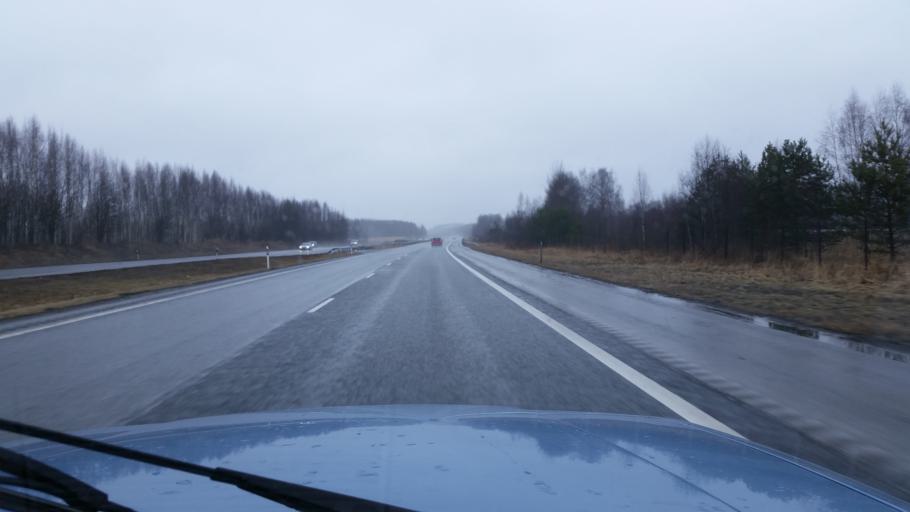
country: FI
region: Haeme
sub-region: Haemeenlinna
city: Janakkala
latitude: 60.8655
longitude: 24.5826
